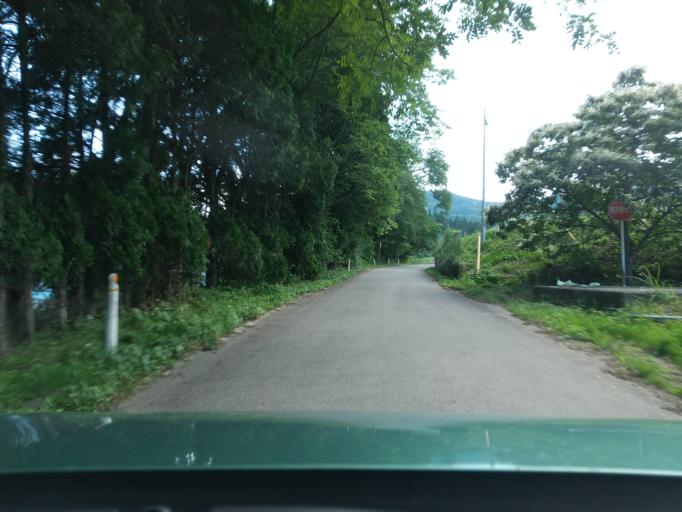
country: JP
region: Iwate
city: Ichinoseki
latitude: 39.0051
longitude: 141.2218
